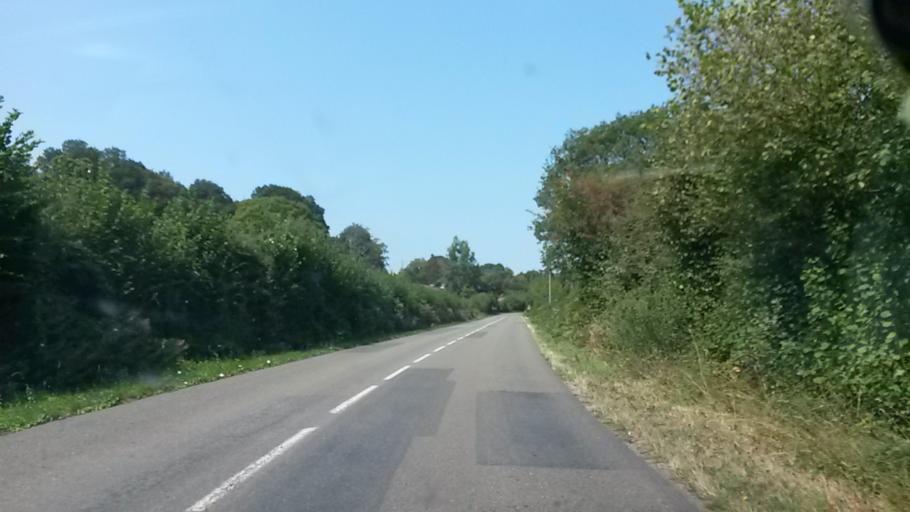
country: FR
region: Pays de la Loire
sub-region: Departement de la Mayenne
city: Saint-Pierre-des-Nids
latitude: 48.3655
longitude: -0.1637
